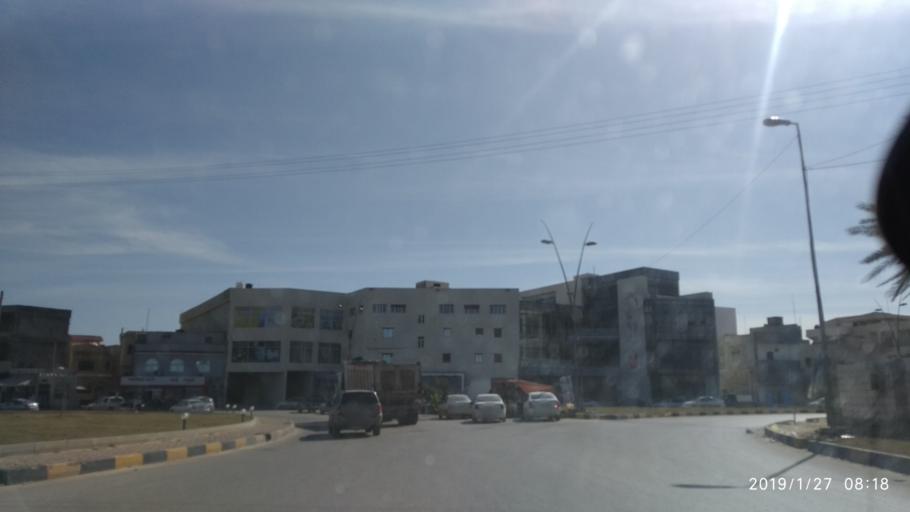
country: LY
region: Tripoli
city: Tagiura
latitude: 32.8938
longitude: 13.3429
